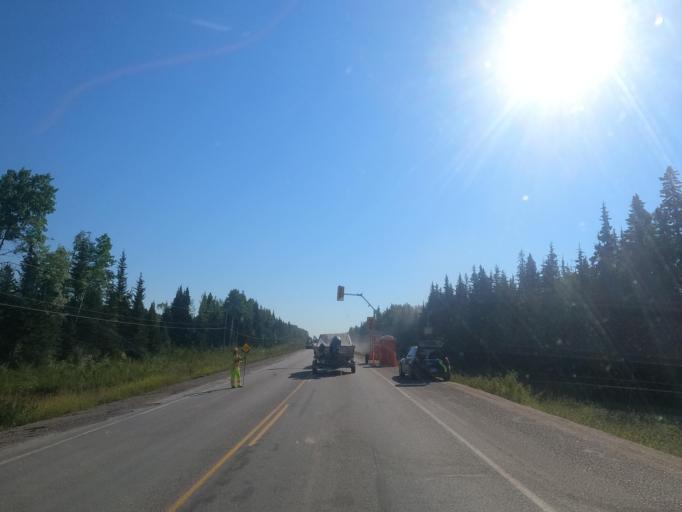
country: CA
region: British Columbia
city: Burns Lake
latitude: 54.1018
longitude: -125.3312
